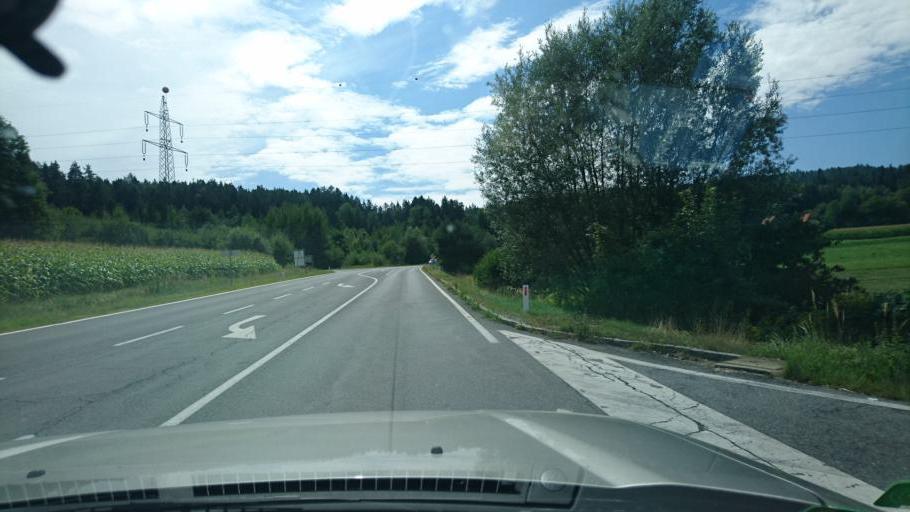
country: AT
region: Carinthia
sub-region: Villach Stadt
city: Villach
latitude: 46.5970
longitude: 13.8843
